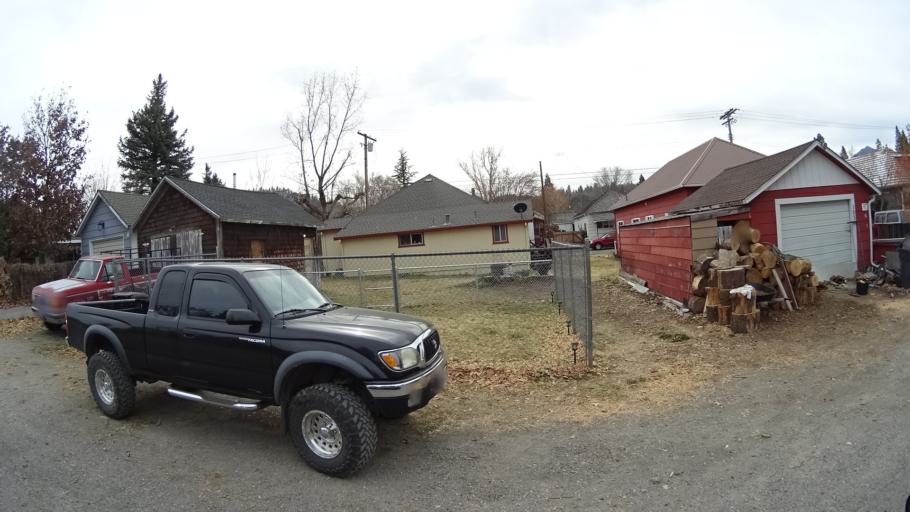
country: US
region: California
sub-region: Siskiyou County
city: Weed
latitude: 41.4257
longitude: -122.3854
